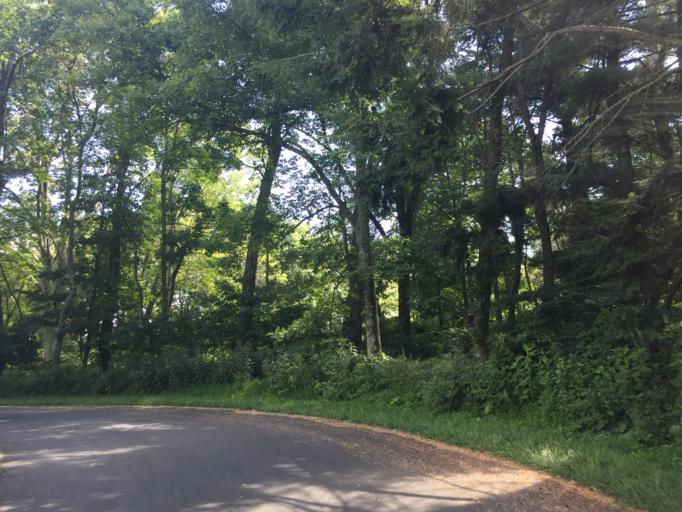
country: US
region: Virginia
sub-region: Rappahannock County
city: Washington
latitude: 38.7387
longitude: -78.3104
